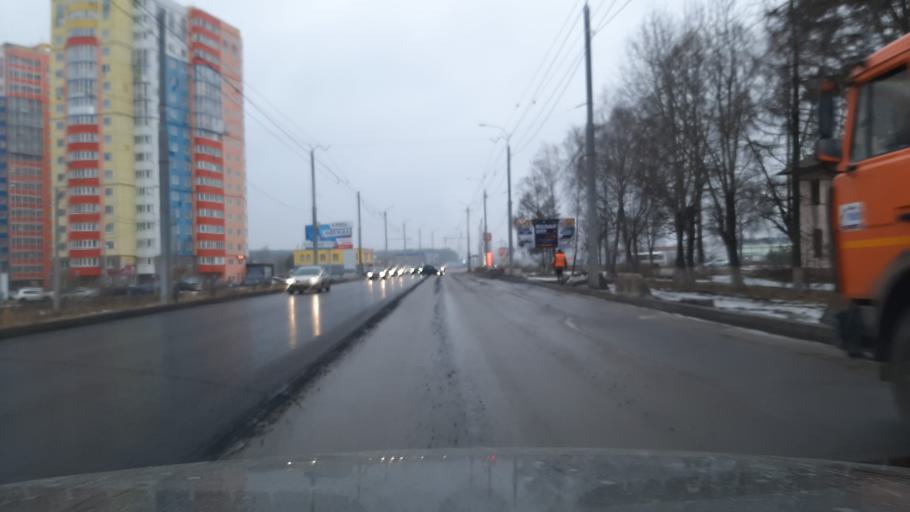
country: RU
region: Ivanovo
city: Kokhma
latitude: 56.9418
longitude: 41.0608
